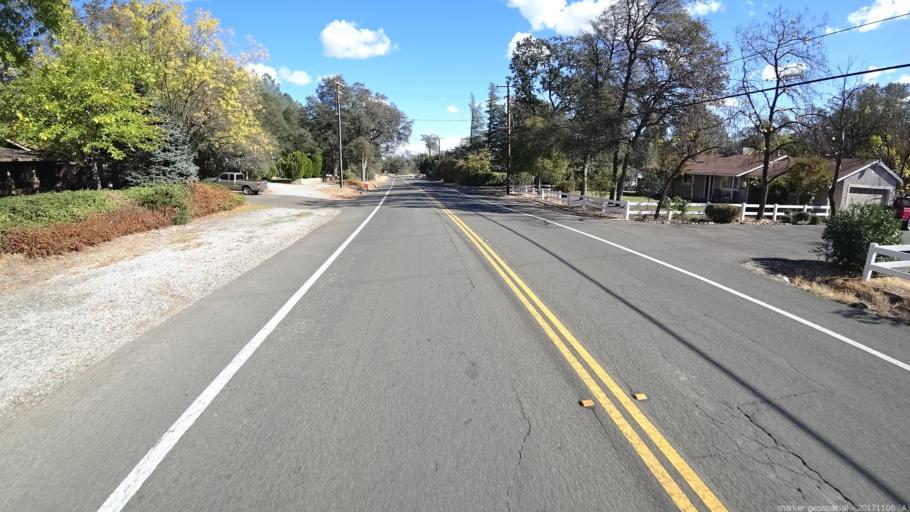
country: US
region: California
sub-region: Shasta County
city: Palo Cedro
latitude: 40.5877
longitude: -122.3099
